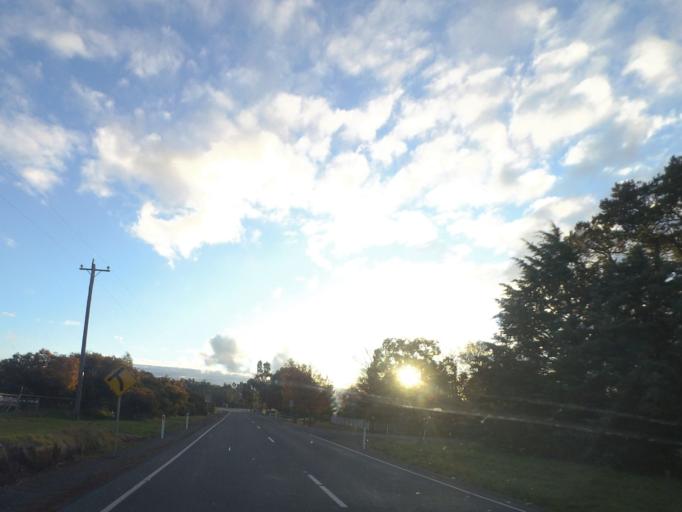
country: AU
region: Victoria
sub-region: Mount Alexander
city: Castlemaine
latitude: -37.2853
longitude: 144.5022
